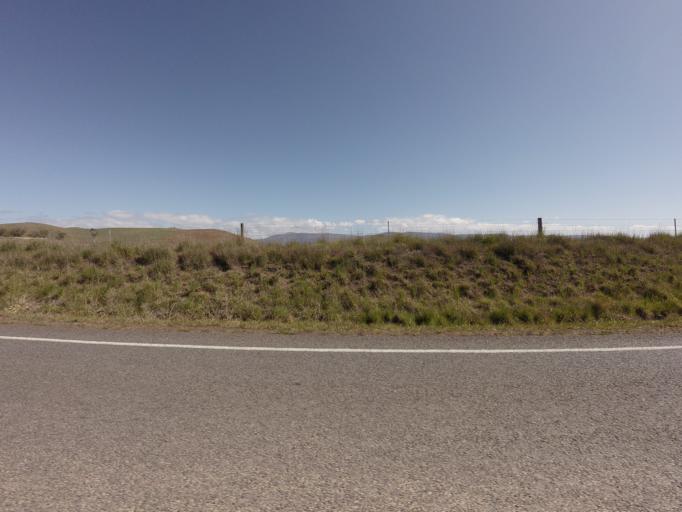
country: AU
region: Tasmania
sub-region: Derwent Valley
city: New Norfolk
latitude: -42.5433
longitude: 146.7748
